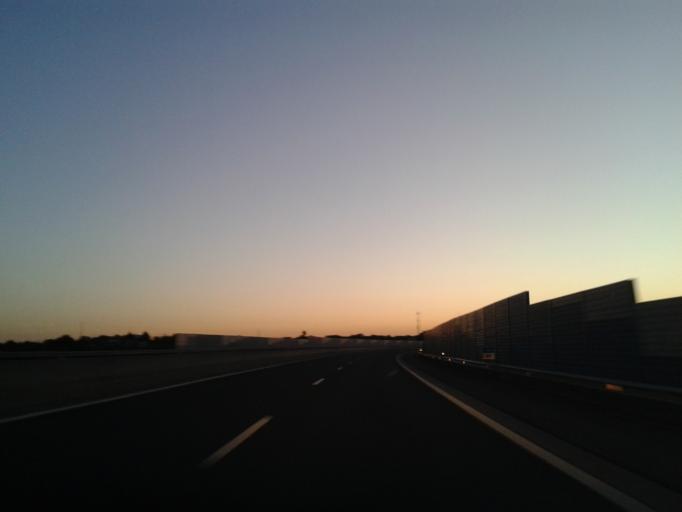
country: PT
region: Faro
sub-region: Albufeira
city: Guia
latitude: 37.1389
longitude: -8.2825
